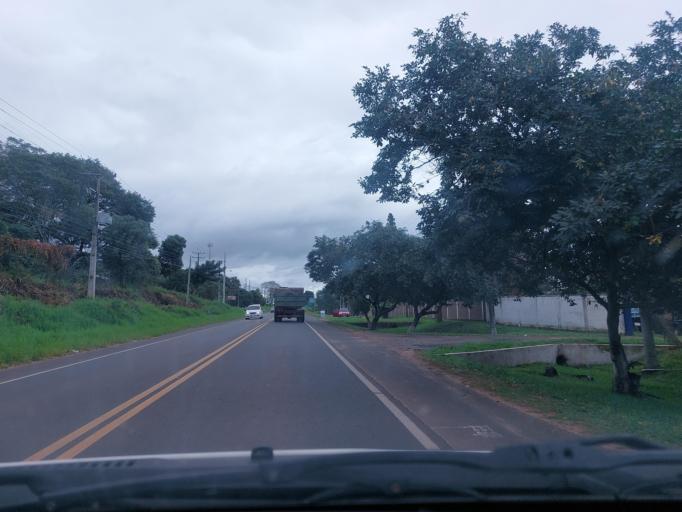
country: PY
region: San Pedro
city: Guayaybi
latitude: -24.6645
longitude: -56.4157
